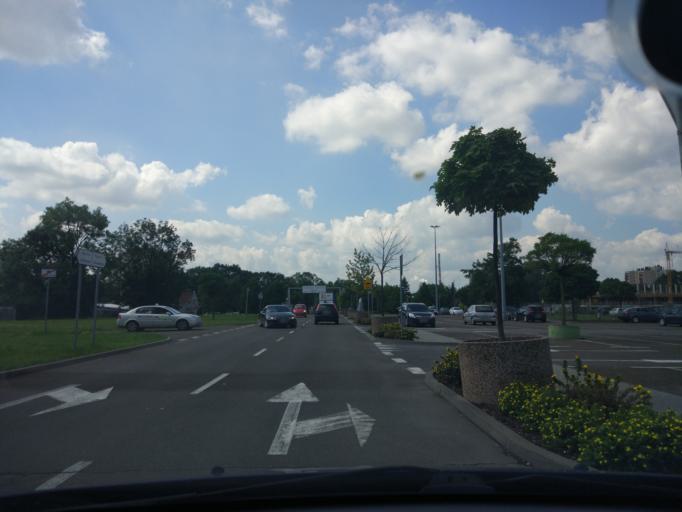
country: PL
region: Lesser Poland Voivodeship
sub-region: Krakow
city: Krakow
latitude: 50.0770
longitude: 20.0188
